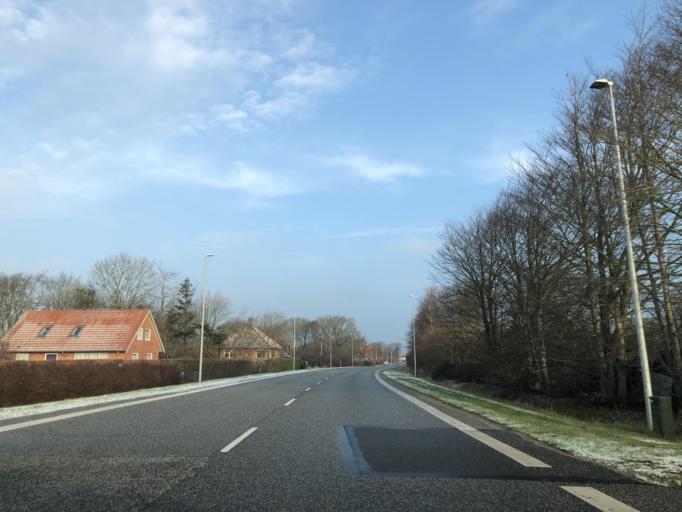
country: DK
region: Central Jutland
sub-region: Ringkobing-Skjern Kommune
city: Tarm
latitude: 55.8978
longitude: 8.5144
